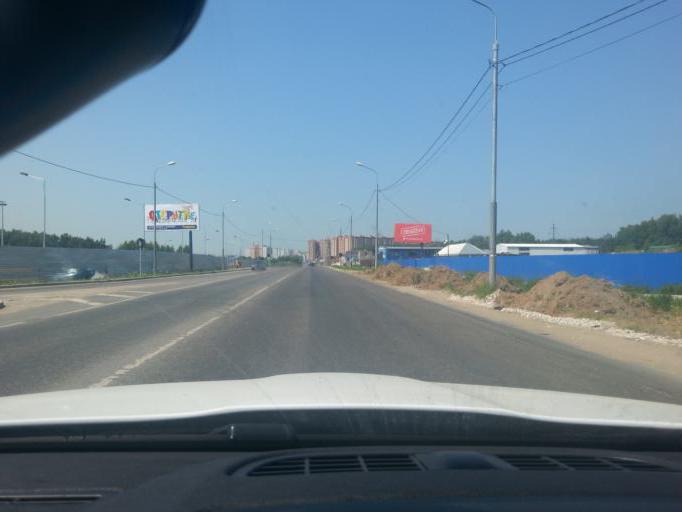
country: RU
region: Moskovskaya
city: Zheleznodorozhnyy
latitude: 55.7256
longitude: 37.9951
